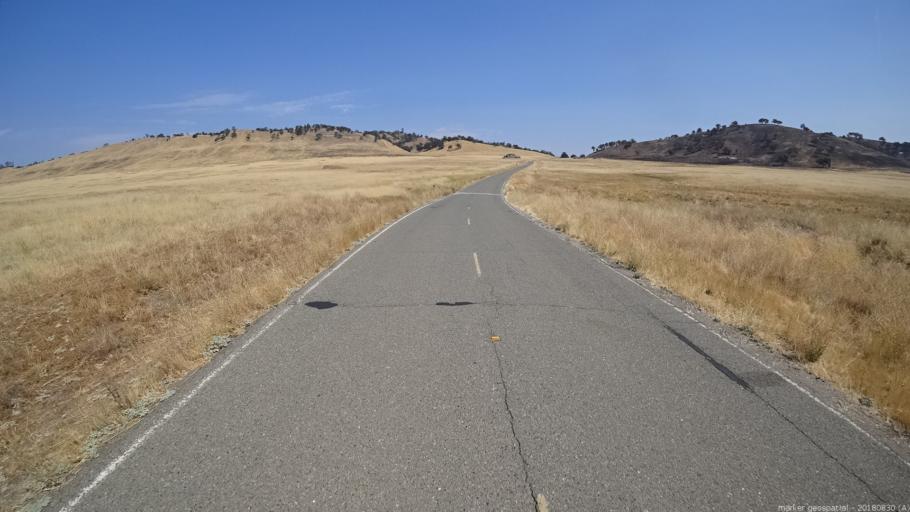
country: US
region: California
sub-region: Monterey County
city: King City
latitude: 35.9661
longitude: -121.2765
